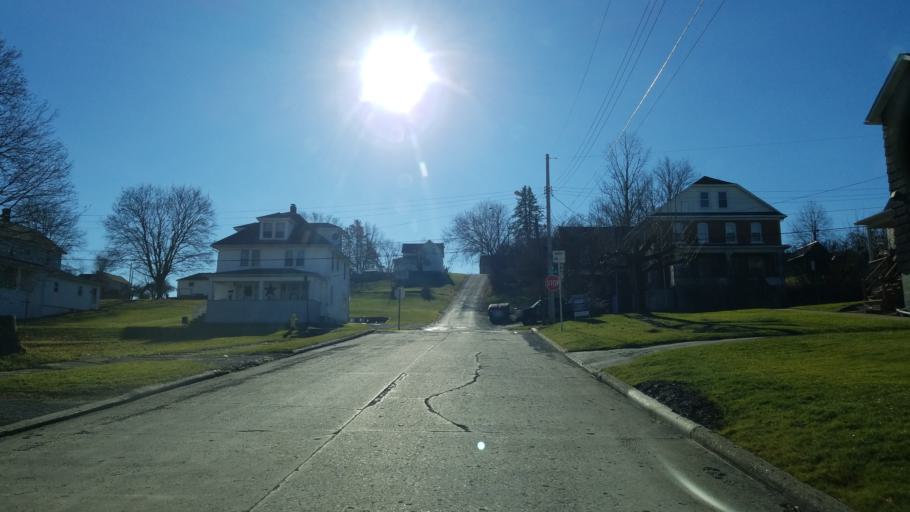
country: US
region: Pennsylvania
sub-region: Clearfield County
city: Sandy
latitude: 41.1212
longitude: -78.7763
